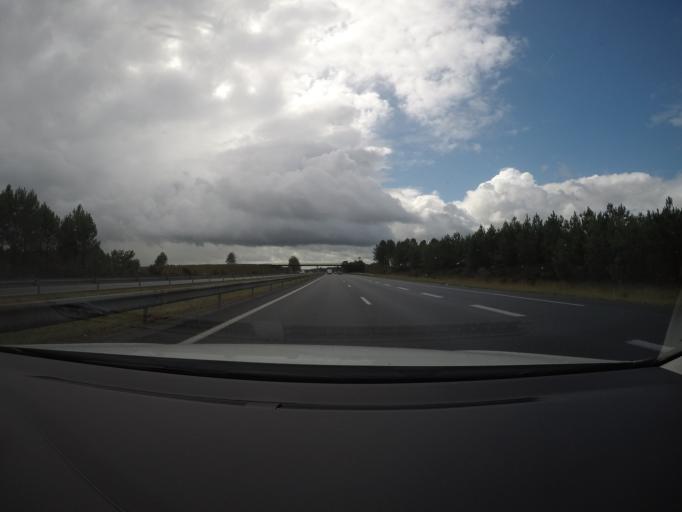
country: FR
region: Aquitaine
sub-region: Departement de la Gironde
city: Marcheprime
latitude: 44.6217
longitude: -0.8499
